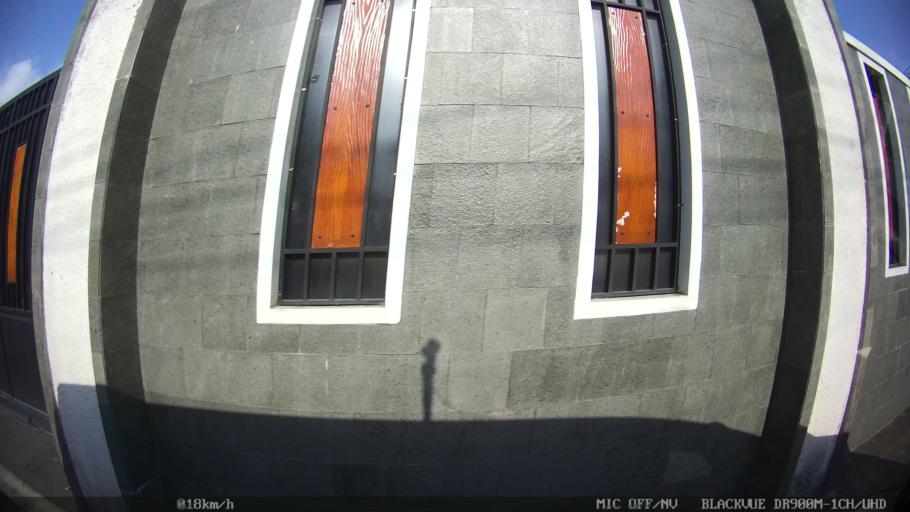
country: ID
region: Daerah Istimewa Yogyakarta
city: Yogyakarta
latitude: -7.7997
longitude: 110.3483
